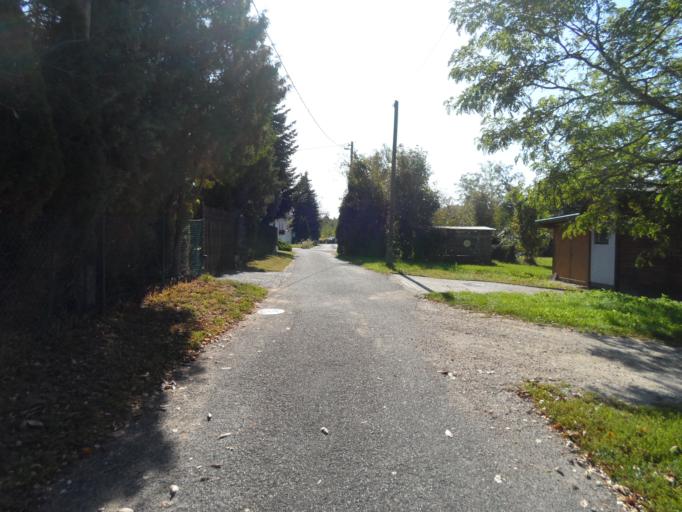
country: HU
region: Veszprem
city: Papa
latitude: 47.2298
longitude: 17.5428
